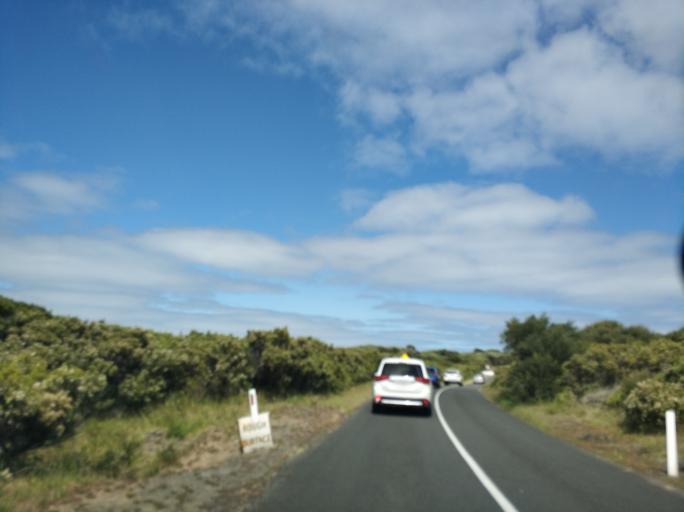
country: AU
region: Victoria
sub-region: Colac-Otway
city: Apollo Bay
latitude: -38.8525
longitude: 143.5240
